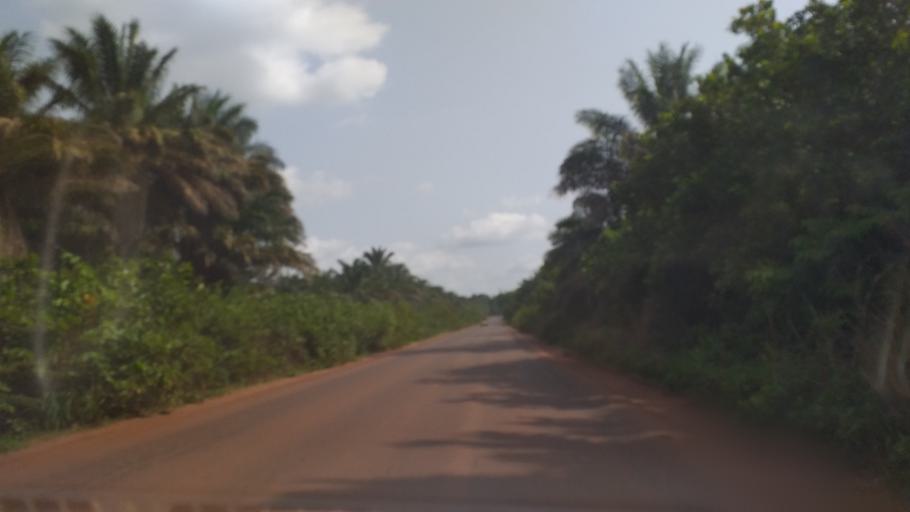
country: GN
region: Boke
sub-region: Boke Prefecture
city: Sangueya
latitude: 10.8258
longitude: -14.3707
